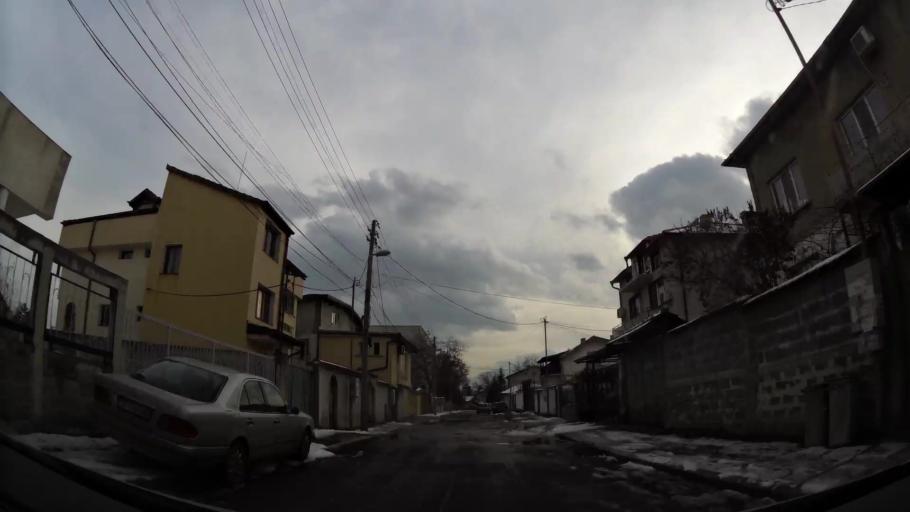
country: BG
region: Sofia-Capital
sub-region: Stolichna Obshtina
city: Sofia
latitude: 42.7176
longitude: 23.3464
